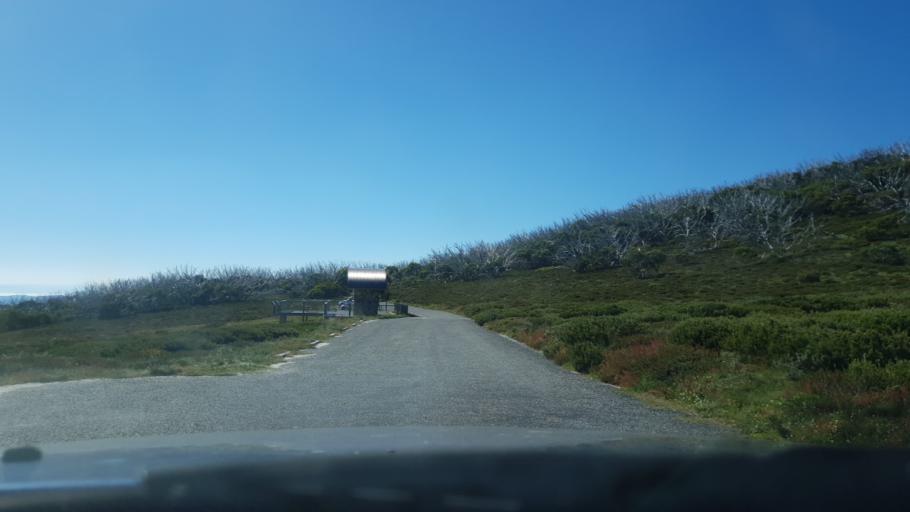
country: AU
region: Victoria
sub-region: Alpine
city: Mount Beauty
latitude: -36.8930
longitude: 147.3008
